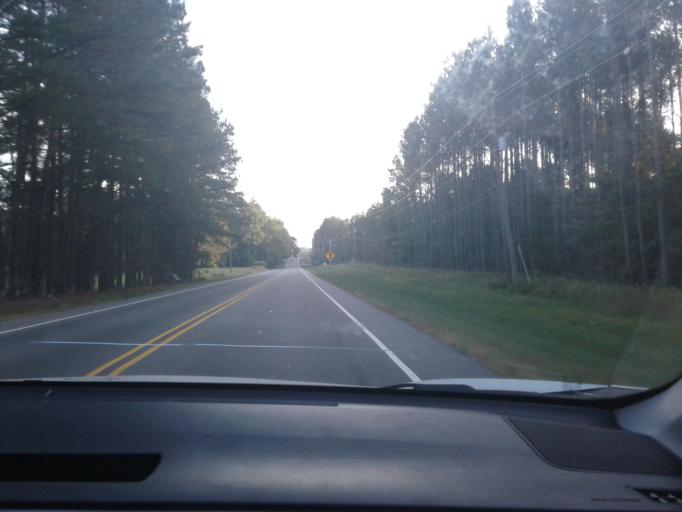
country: US
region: North Carolina
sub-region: Harnett County
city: Lillington
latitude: 35.4437
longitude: -78.8277
